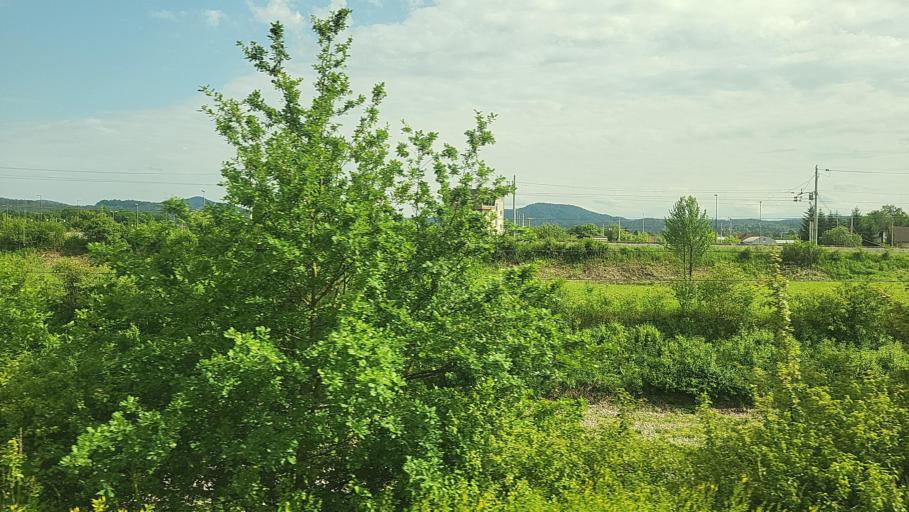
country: SI
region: Dol pri Ljubljani
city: Dol pri Ljubljani
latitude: 46.0603
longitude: 14.5904
